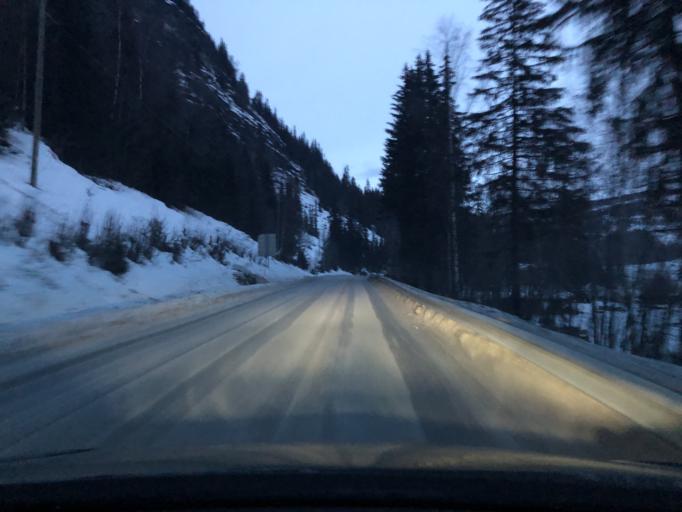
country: NO
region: Oppland
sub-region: Nord-Aurdal
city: Fagernes
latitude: 61.0002
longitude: 9.2098
